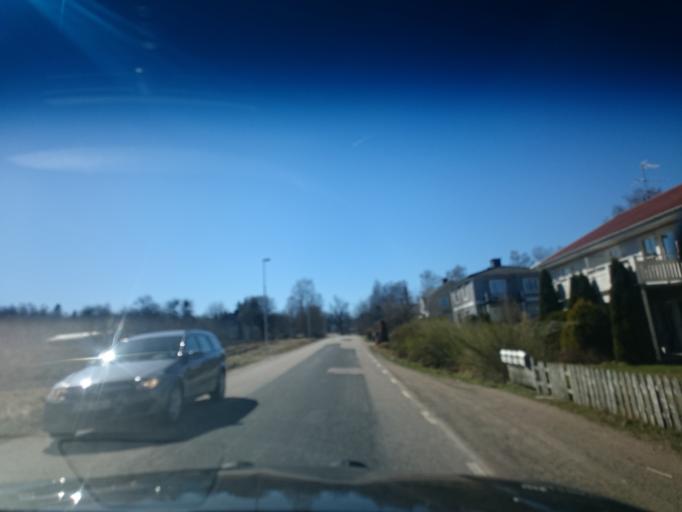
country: SE
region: Joenkoeping
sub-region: Vetlanda Kommun
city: Vetlanda
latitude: 57.2933
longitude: 15.1134
